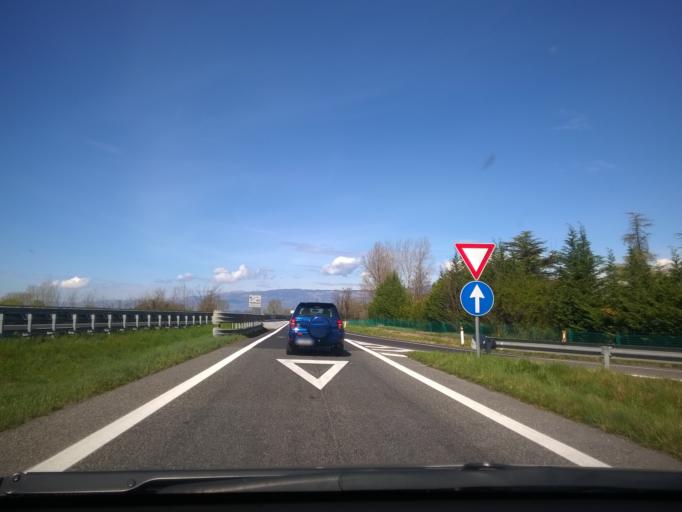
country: IT
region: Friuli Venezia Giulia
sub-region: Provincia di Pordenone
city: Azzano Decimo
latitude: 45.9206
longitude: 12.7000
